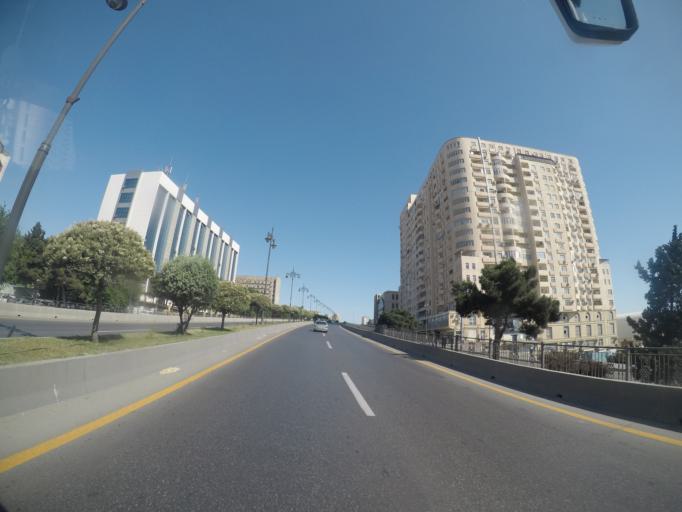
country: AZ
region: Baki
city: Khodzhi-Gasan
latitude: 40.4014
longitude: 49.8096
